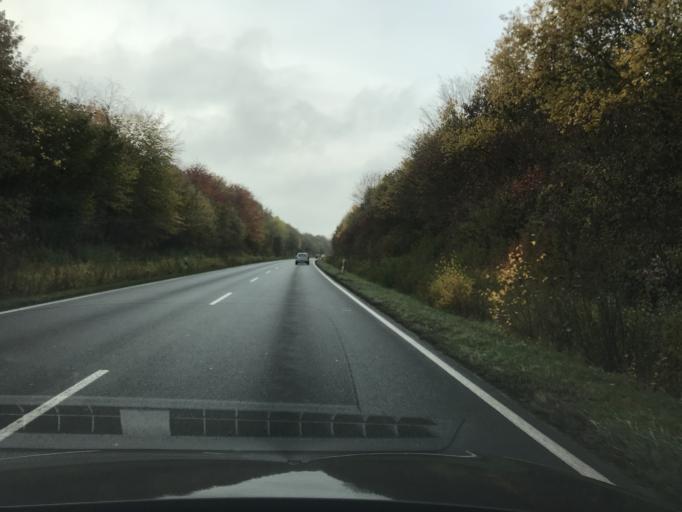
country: DE
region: North Rhine-Westphalia
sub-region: Regierungsbezirk Arnsberg
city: Hamm
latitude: 51.7036
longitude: 7.7334
